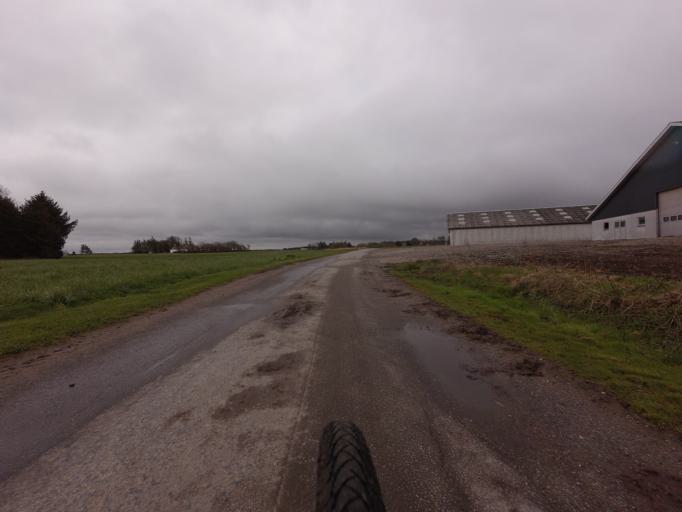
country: DK
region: North Denmark
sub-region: Jammerbugt Kommune
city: Pandrup
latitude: 57.3349
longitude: 9.7860
